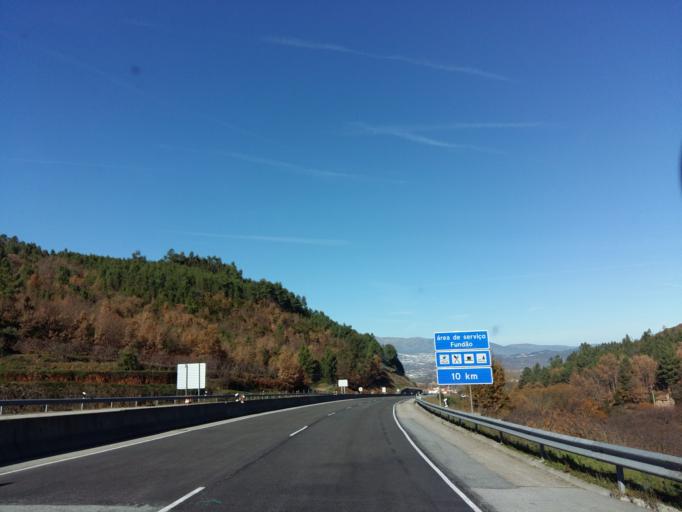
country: PT
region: Castelo Branco
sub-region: Concelho do Fundao
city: Fundao
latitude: 40.1201
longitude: -7.4772
